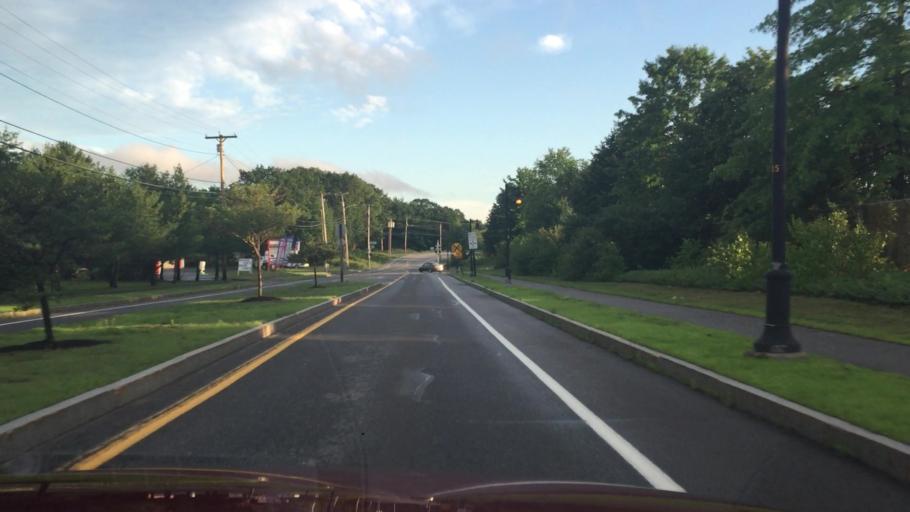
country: US
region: Maine
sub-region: Cumberland County
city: South Portland Gardens
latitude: 43.6703
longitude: -70.3223
